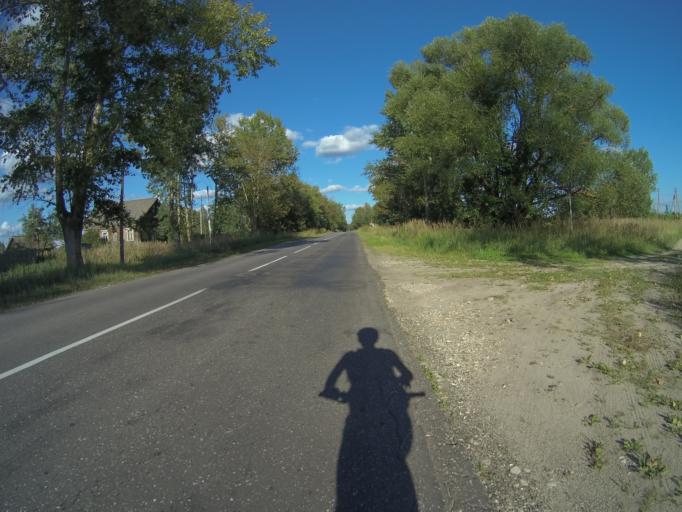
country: RU
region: Vladimir
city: Gusevskiy
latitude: 55.5744
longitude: 40.4986
